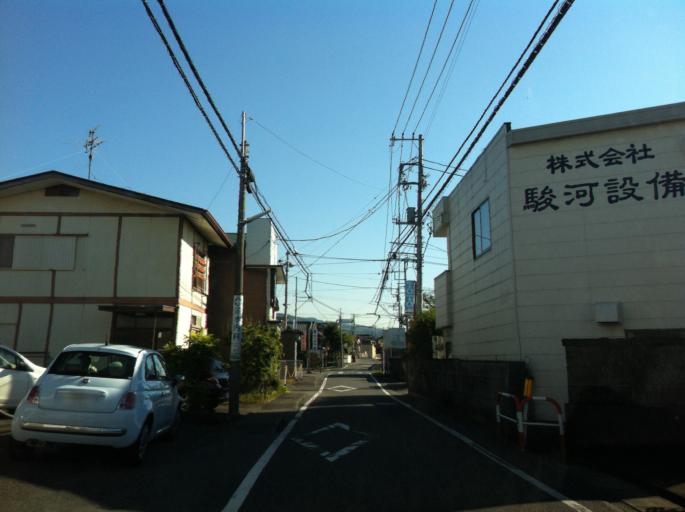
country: JP
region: Shizuoka
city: Fuji
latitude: 35.1652
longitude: 138.7220
